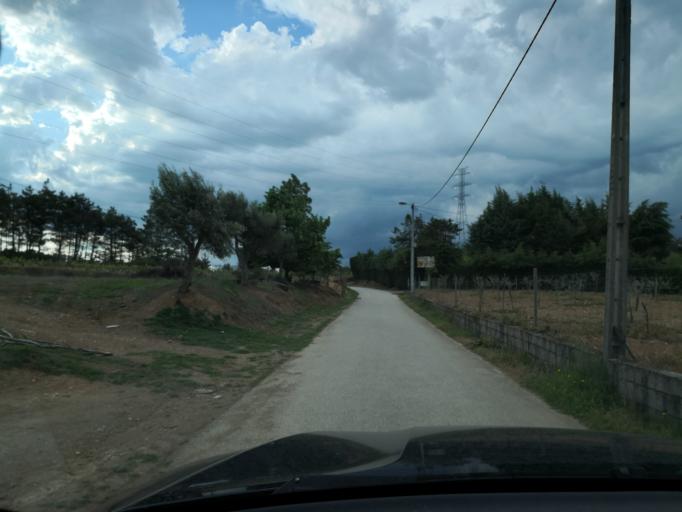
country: PT
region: Vila Real
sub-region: Sabrosa
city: Vilela
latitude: 41.2208
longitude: -7.6689
